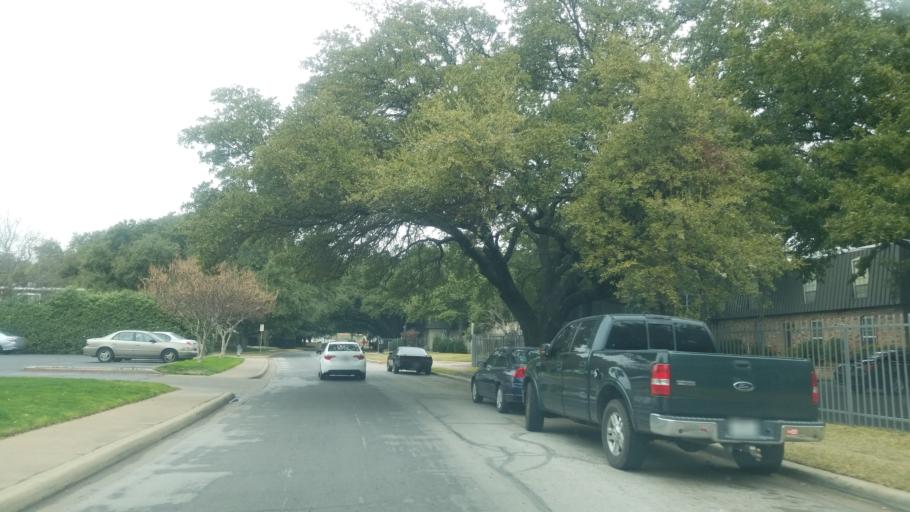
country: US
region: Texas
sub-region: Dallas County
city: Highland Park
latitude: 32.8177
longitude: -96.8301
